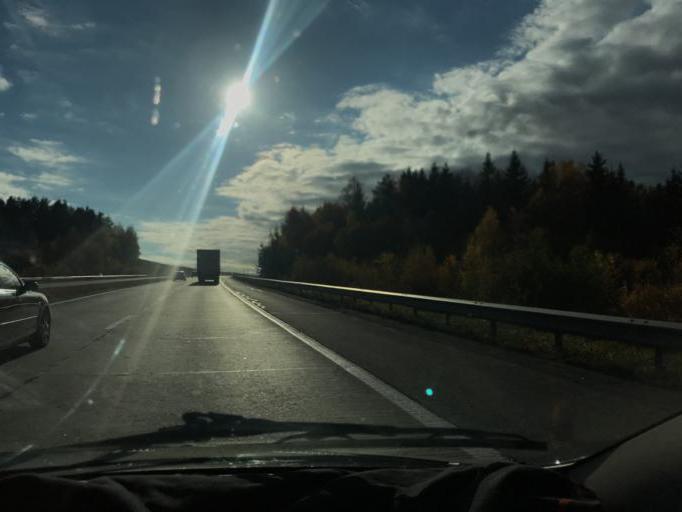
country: BY
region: Minsk
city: Lahoysk
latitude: 54.1065
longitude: 27.7997
